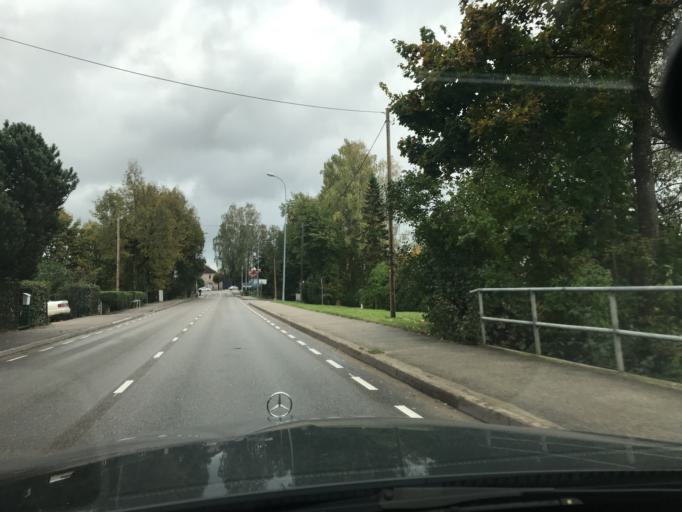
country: EE
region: Valgamaa
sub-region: Torva linn
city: Torva
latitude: 58.0046
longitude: 25.9201
